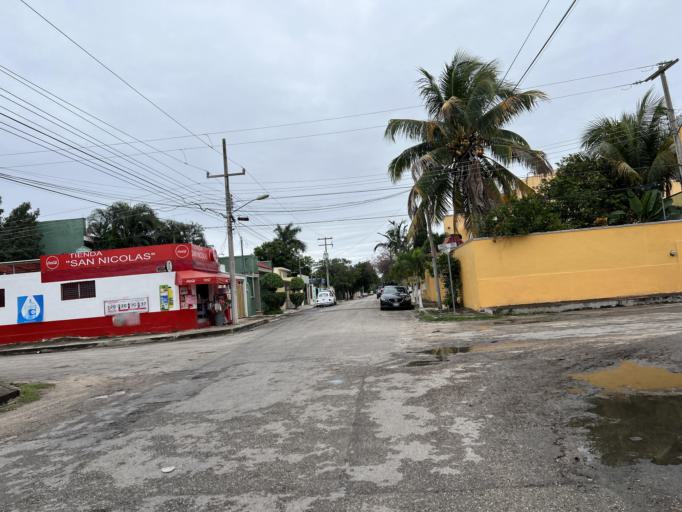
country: MX
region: Yucatan
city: Merida
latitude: 20.9954
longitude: -89.5865
